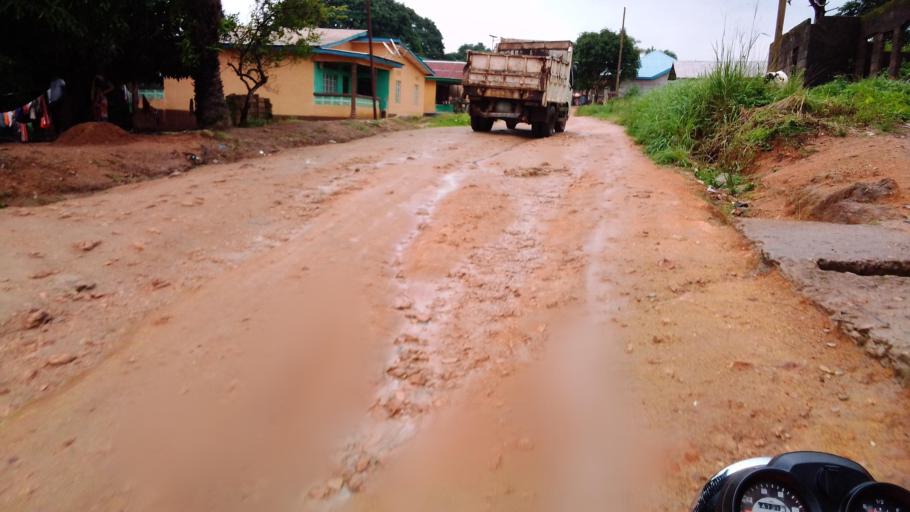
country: SL
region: Eastern Province
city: Kenema
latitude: 7.8946
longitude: -11.1868
